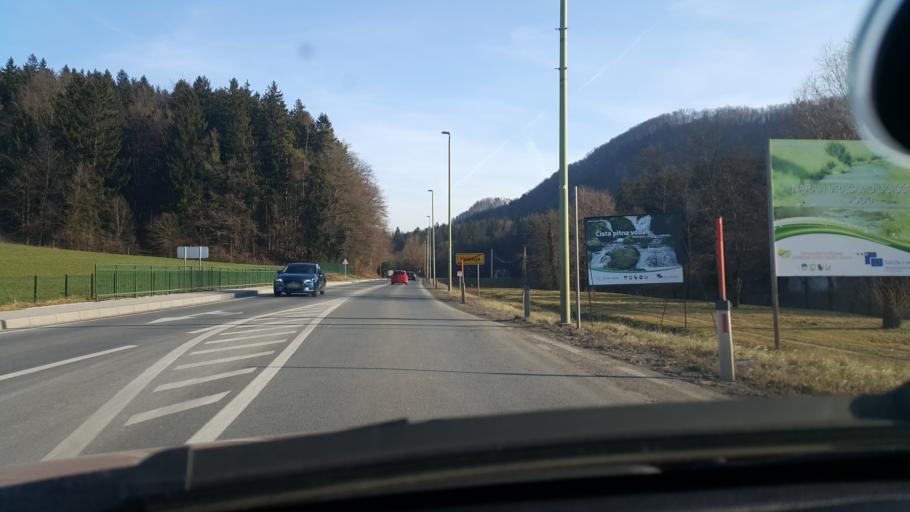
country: SI
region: Velenje
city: Velenje
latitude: 46.3551
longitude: 15.1181
